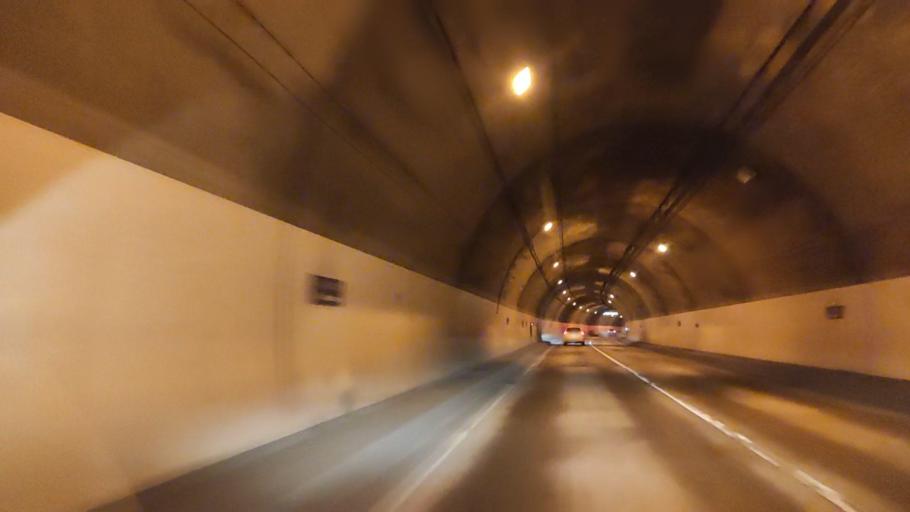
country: JP
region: Hokkaido
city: Ishikari
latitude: 43.4567
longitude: 141.4081
